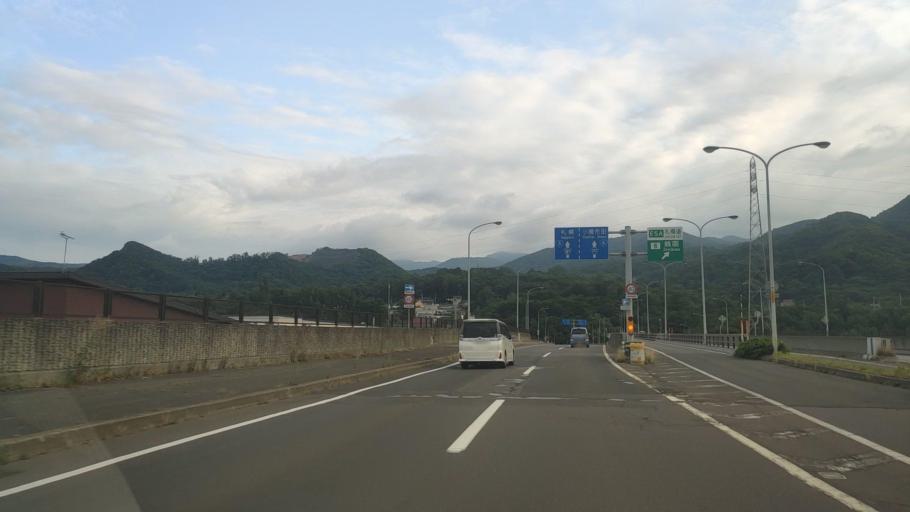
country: JP
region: Hokkaido
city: Otaru
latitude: 43.1391
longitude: 141.1788
